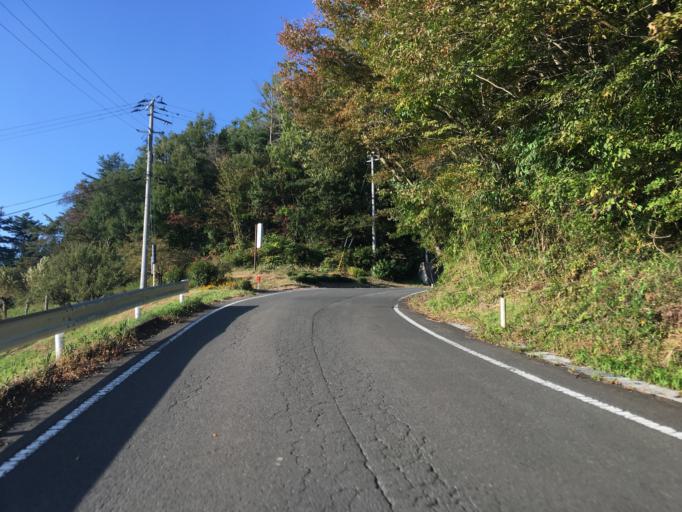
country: JP
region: Fukushima
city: Fukushima-shi
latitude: 37.6447
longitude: 140.5758
